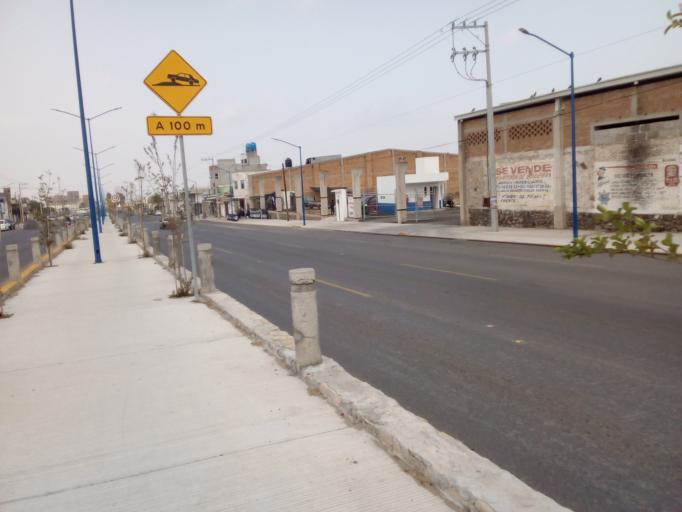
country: MX
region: Guerrero
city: San Luis de la Paz
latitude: 21.2883
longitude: -100.5143
